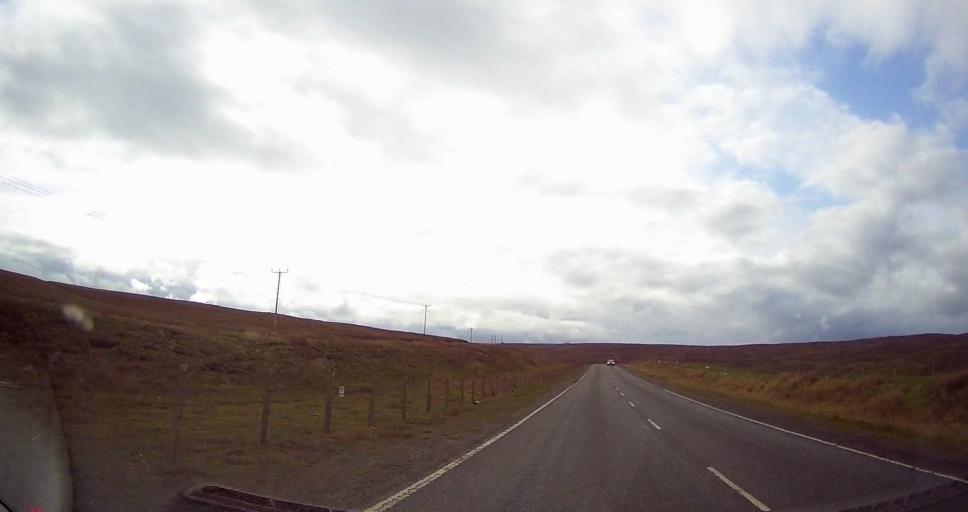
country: GB
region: Scotland
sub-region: Shetland Islands
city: Lerwick
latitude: 60.4433
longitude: -1.2357
